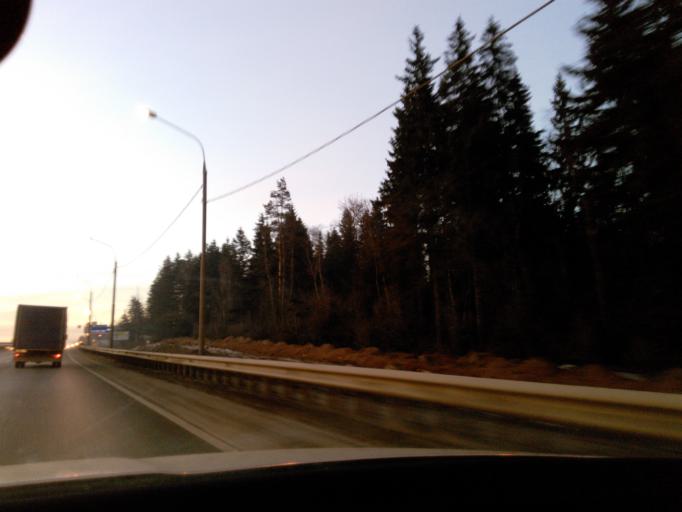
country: RU
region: Moskovskaya
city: Rzhavki
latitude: 55.9923
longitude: 37.2635
